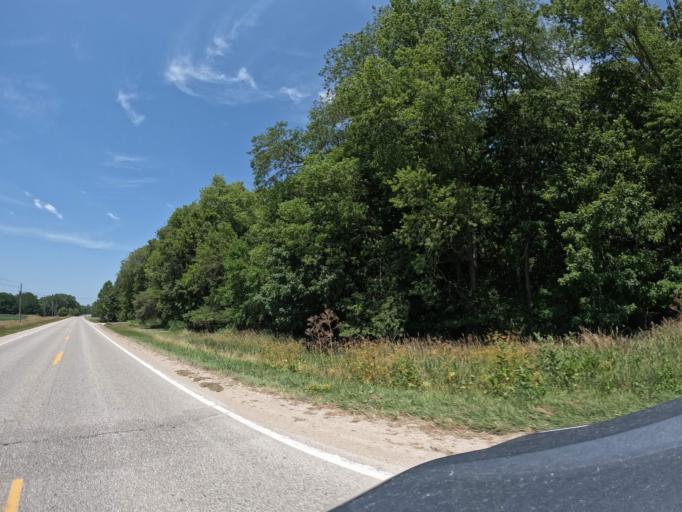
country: US
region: Iowa
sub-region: Henry County
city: Mount Pleasant
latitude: 40.9371
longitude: -91.6086
